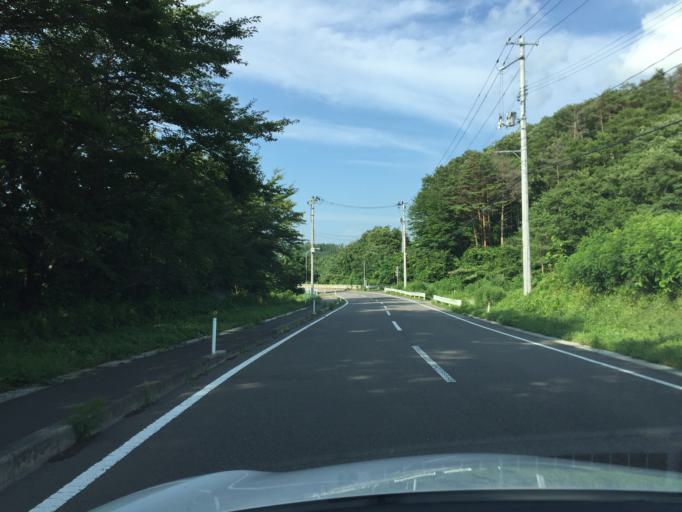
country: JP
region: Fukushima
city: Miharu
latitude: 37.4146
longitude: 140.4993
